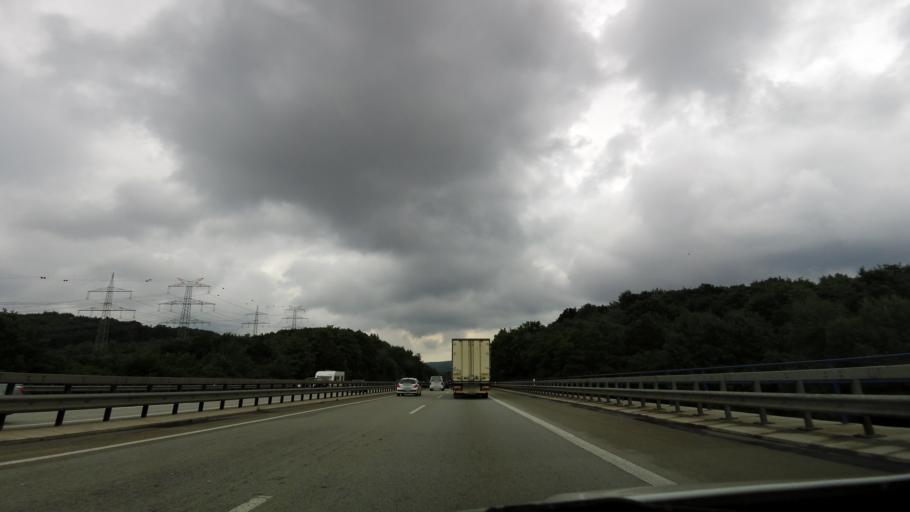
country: DE
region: Rheinland-Pfalz
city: Bad Neuenahr-Ahrweiler
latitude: 50.5627
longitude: 7.1458
